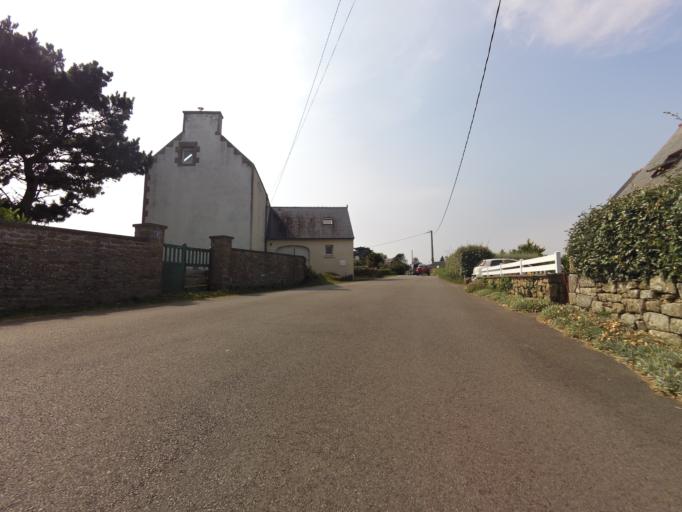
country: FR
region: Brittany
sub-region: Departement du Finistere
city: Esquibien
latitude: 48.0112
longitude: -4.5634
